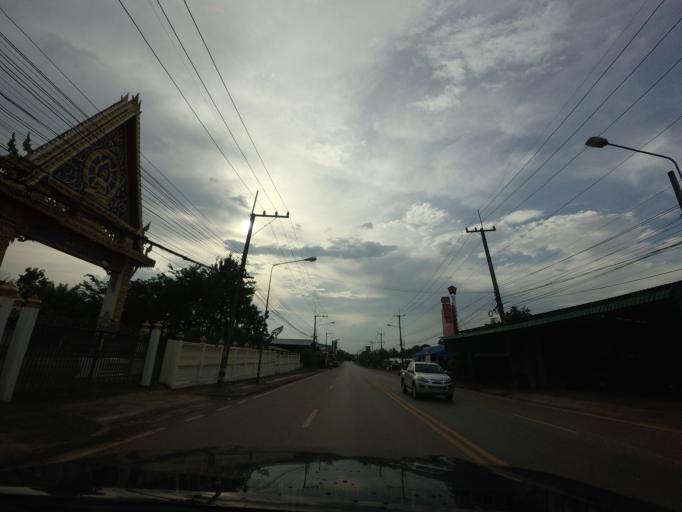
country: TH
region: Changwat Udon Thani
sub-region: Amphoe Ban Phue
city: Ban Phue
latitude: 17.6954
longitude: 102.4583
